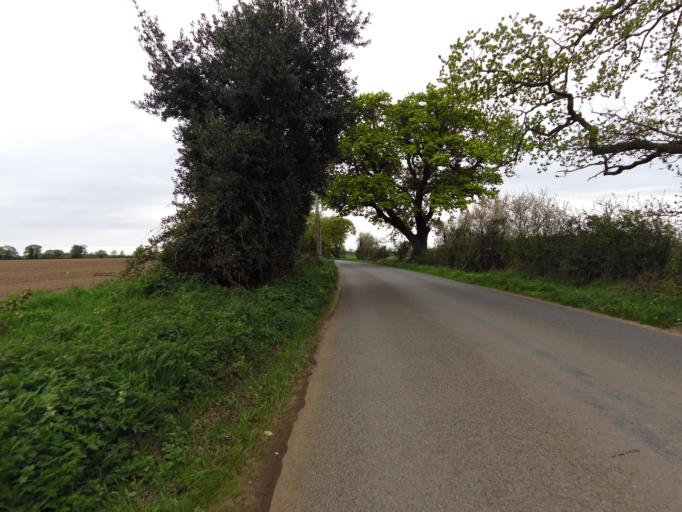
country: GB
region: England
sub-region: Suffolk
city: Kesgrave
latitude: 52.0165
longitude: 1.2227
